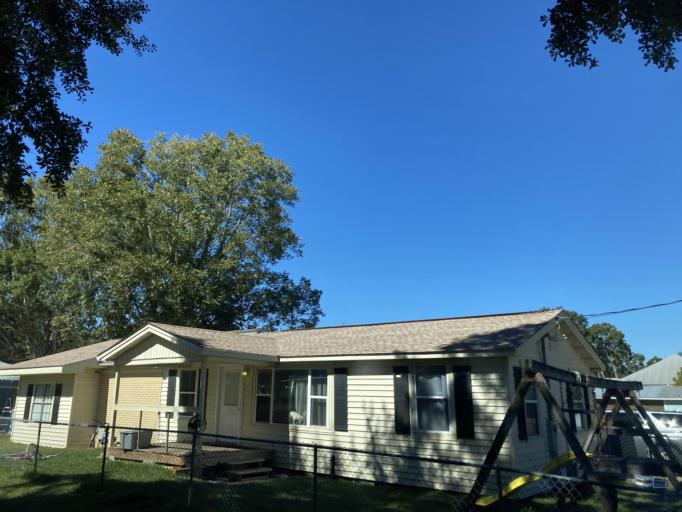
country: US
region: Mississippi
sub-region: Jackson County
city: Ocean Springs
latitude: 30.4104
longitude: -88.8239
